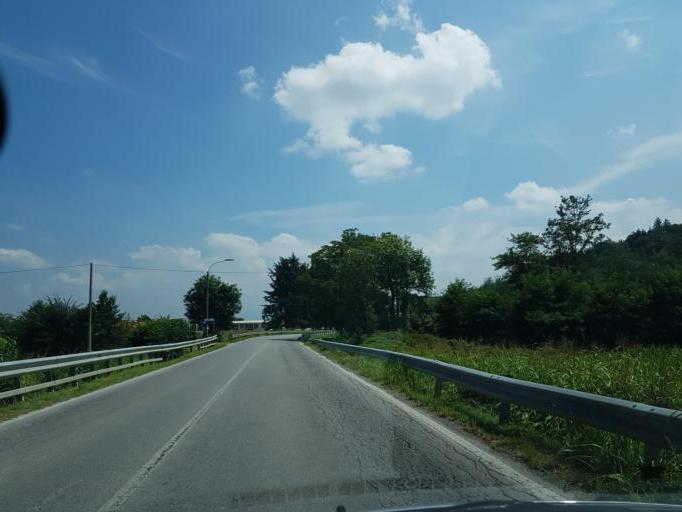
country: IT
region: Piedmont
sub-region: Provincia di Cuneo
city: Caraglio
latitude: 44.4335
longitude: 7.4214
